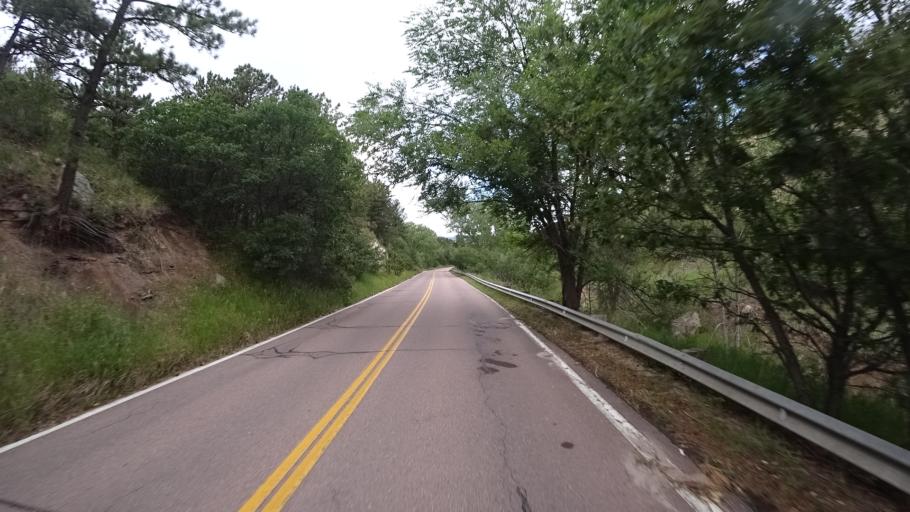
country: US
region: Colorado
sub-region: El Paso County
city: Colorado Springs
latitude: 38.9071
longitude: -104.8332
